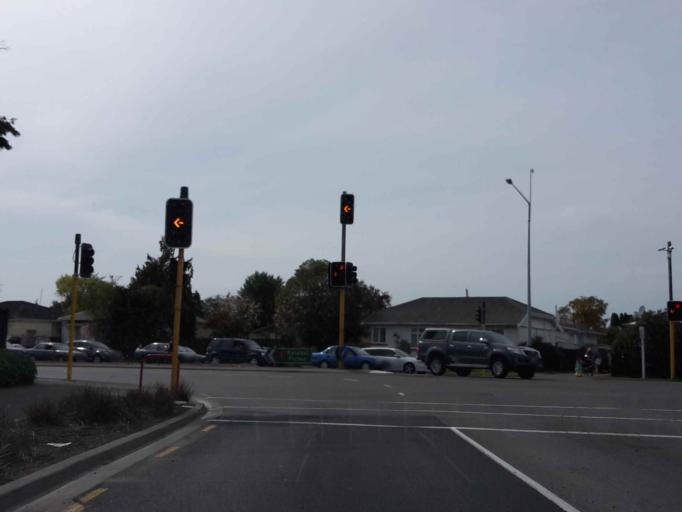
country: NZ
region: Canterbury
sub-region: Waimakariri District
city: Kaiapoi
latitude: -43.4511
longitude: 172.6281
